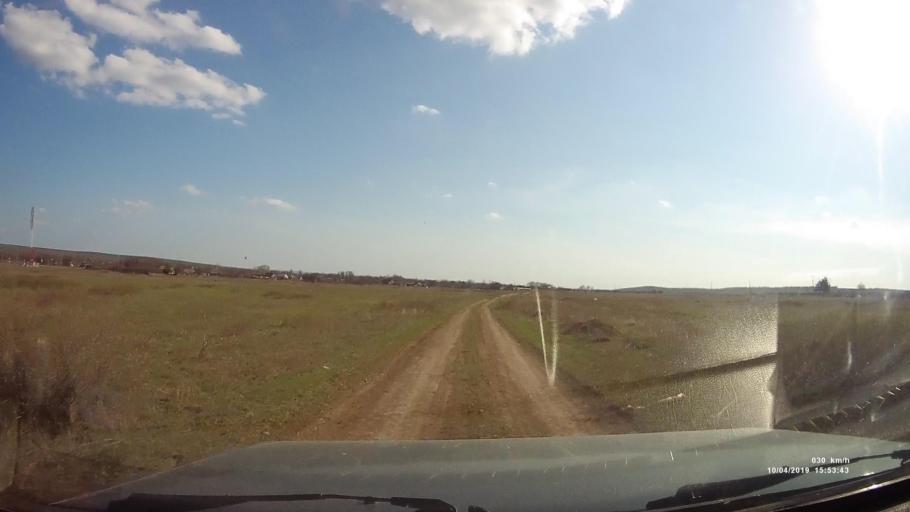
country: RU
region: Rostov
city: Masalovka
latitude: 48.4165
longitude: 40.2587
